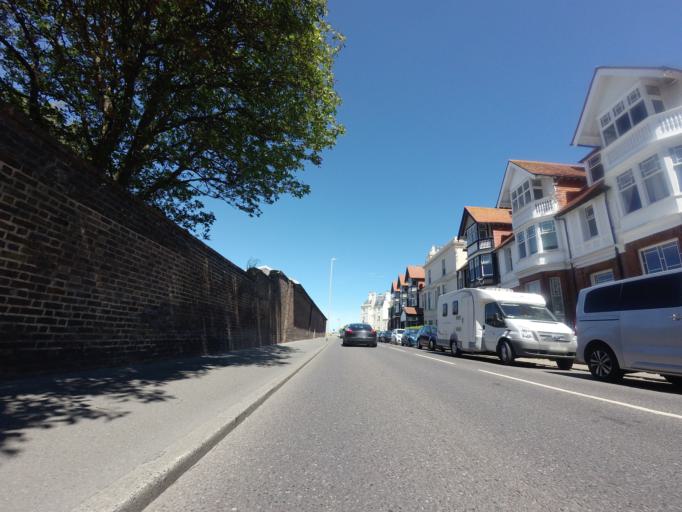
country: GB
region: England
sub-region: Kent
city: Deal
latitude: 51.2114
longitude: 1.4014
